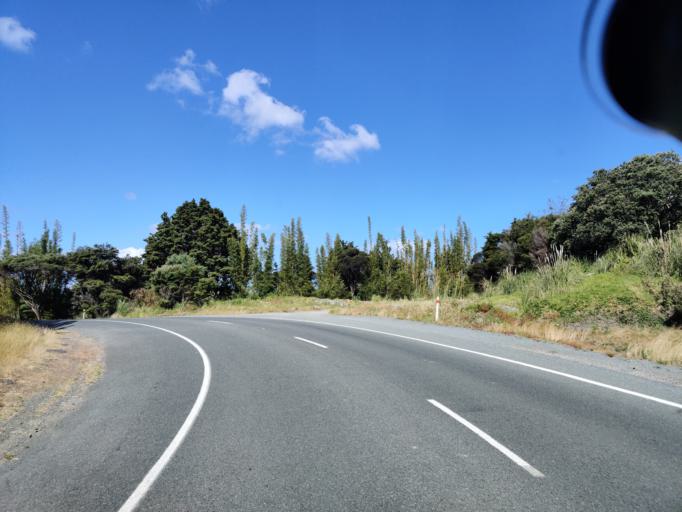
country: NZ
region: Northland
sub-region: Whangarei
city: Ngunguru
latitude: -35.6181
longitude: 174.5161
